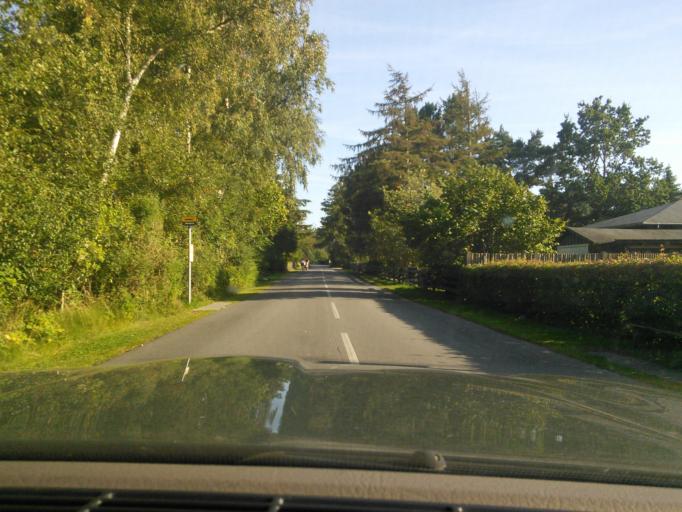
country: DK
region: Capital Region
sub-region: Halsnaes Kommune
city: Liseleje
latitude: 56.0087
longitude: 11.9647
